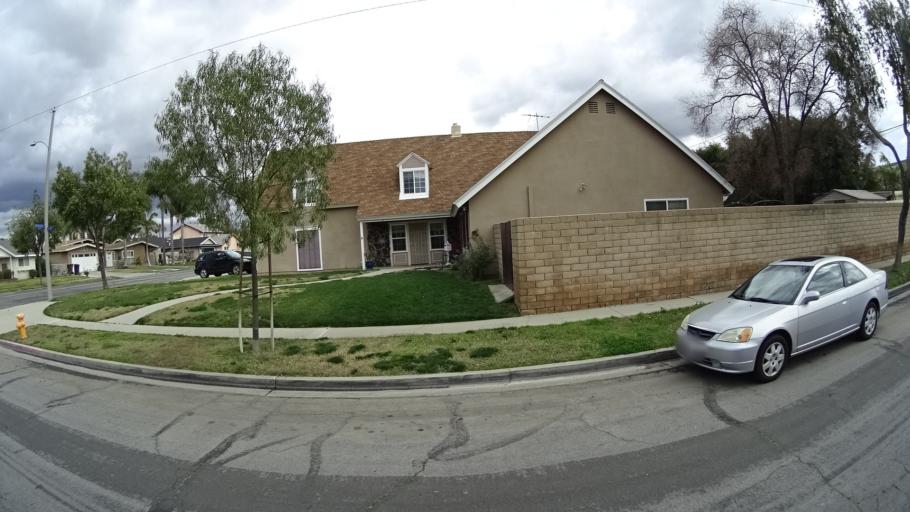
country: US
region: California
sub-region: Orange County
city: Placentia
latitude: 33.8405
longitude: -117.8660
